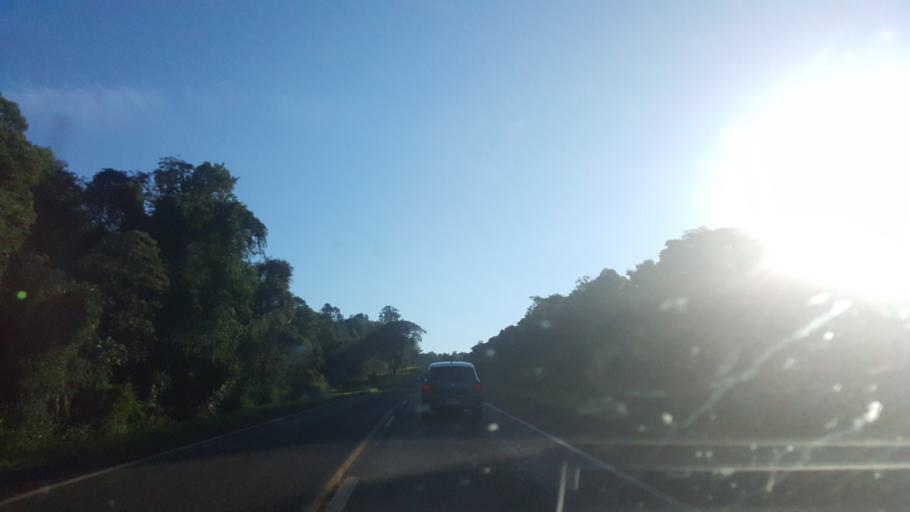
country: AR
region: Misiones
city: El Alcazar
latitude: -26.7194
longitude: -54.8573
